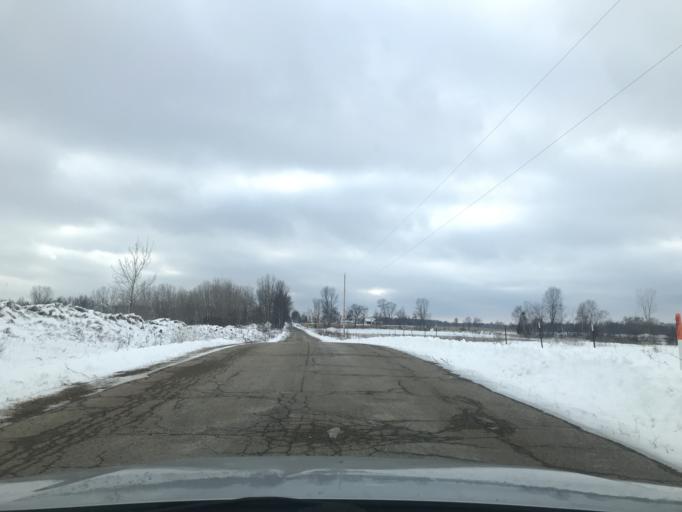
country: US
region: Wisconsin
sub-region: Oconto County
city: Oconto
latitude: 44.9318
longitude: -87.9911
